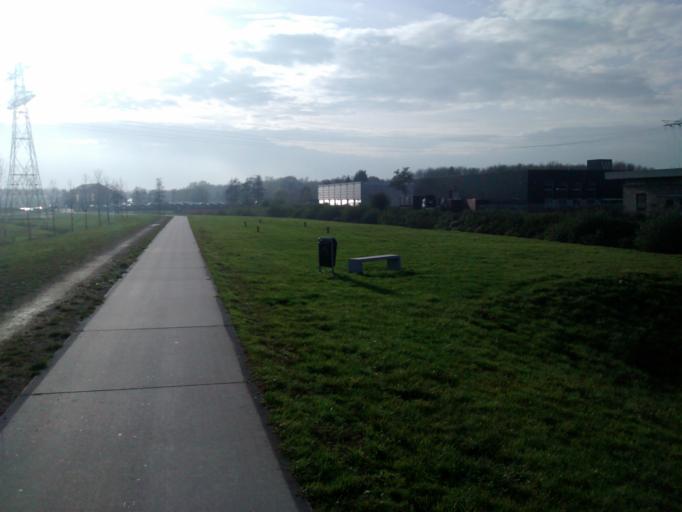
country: NL
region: Utrecht
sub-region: Gemeente Utrecht
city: Lunetten
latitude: 52.0517
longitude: 5.1253
